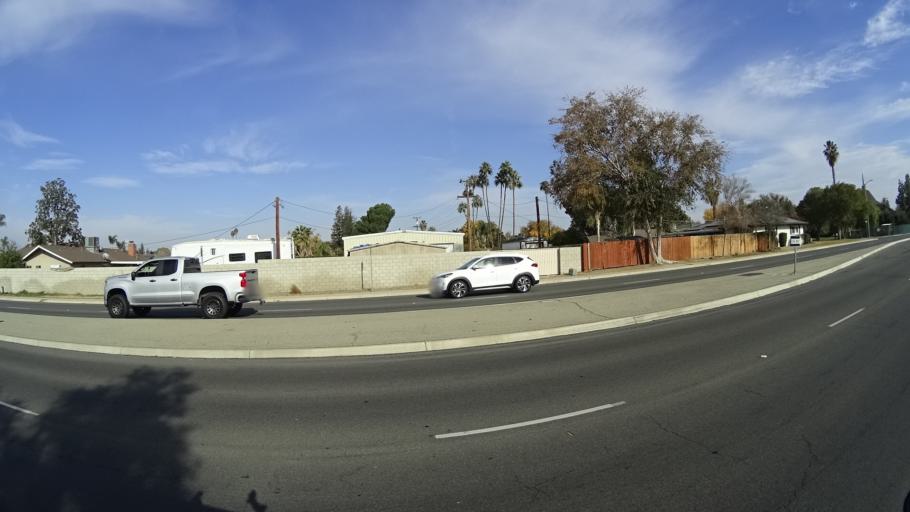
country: US
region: California
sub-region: Kern County
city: Oildale
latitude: 35.4123
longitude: -119.0666
